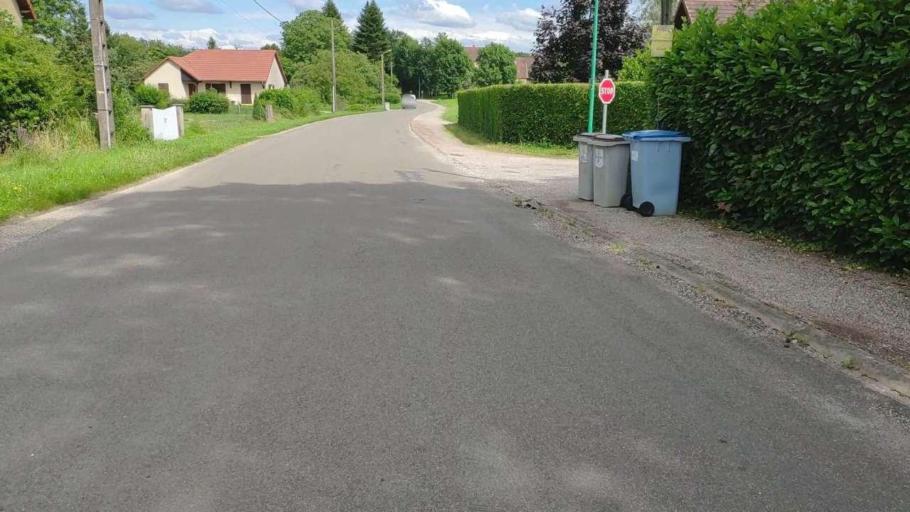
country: FR
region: Franche-Comte
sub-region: Departement du Jura
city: Bletterans
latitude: 46.8032
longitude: 5.4480
